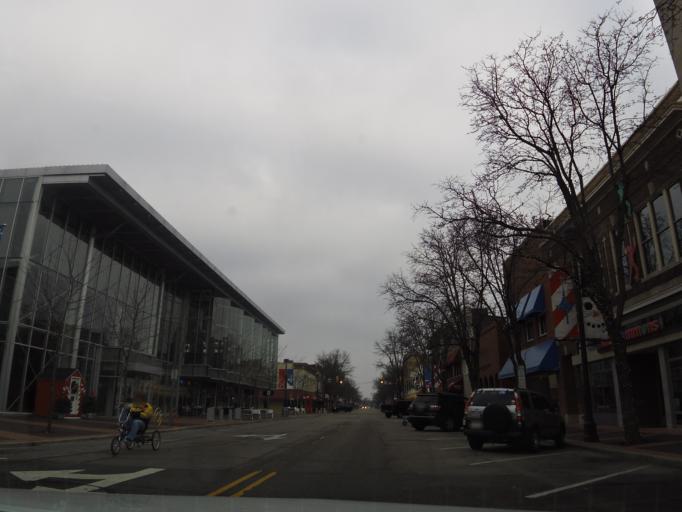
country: US
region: Indiana
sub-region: Bartholomew County
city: Columbus
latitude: 39.2015
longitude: -85.9211
